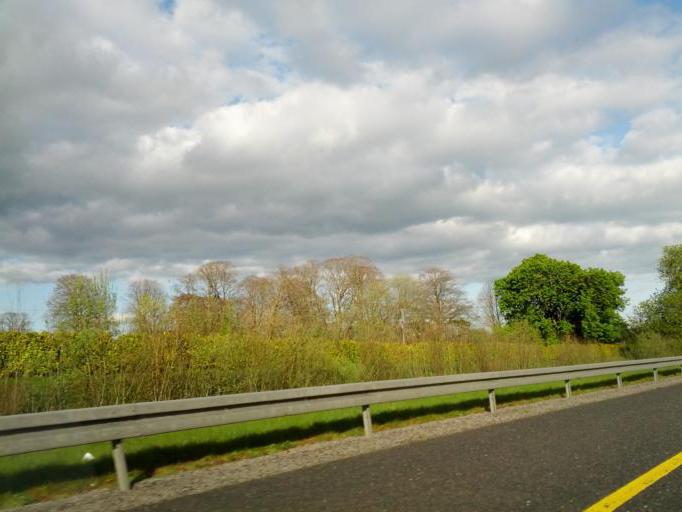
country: IE
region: Leinster
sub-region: An Mhi
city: Longwood
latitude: 53.4242
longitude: -6.9175
